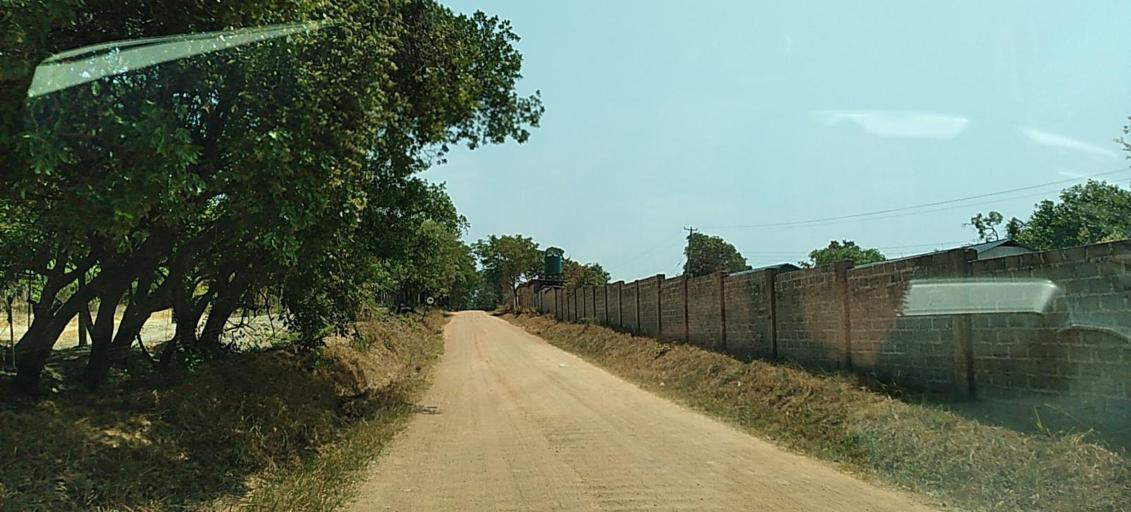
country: ZM
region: Copperbelt
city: Chambishi
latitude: -12.6083
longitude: 27.9529
